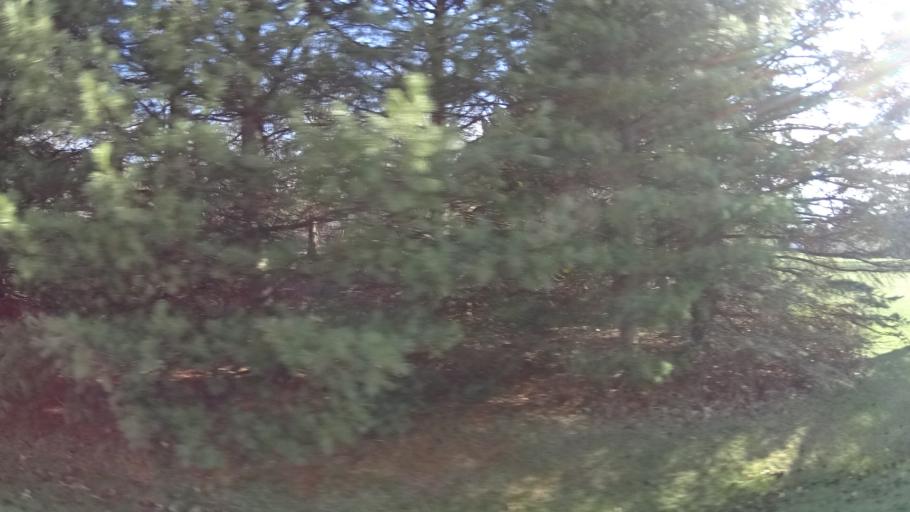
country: US
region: Ohio
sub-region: Lorain County
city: Camden
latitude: 41.1908
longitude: -82.2832
